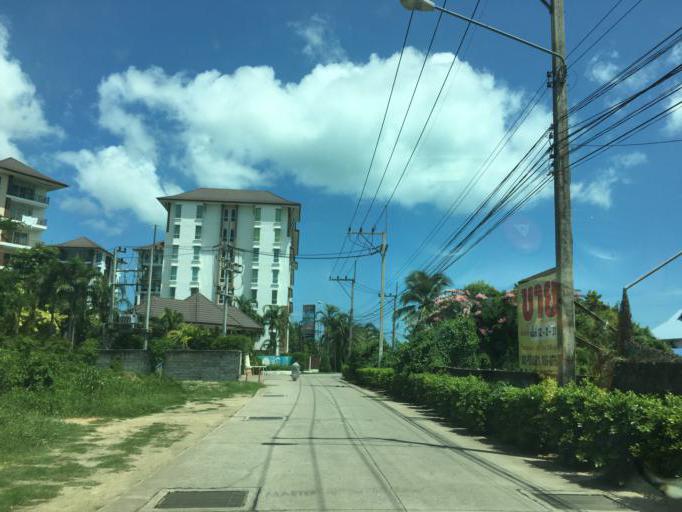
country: TH
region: Chon Buri
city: Sattahip
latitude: 12.7643
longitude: 100.9041
